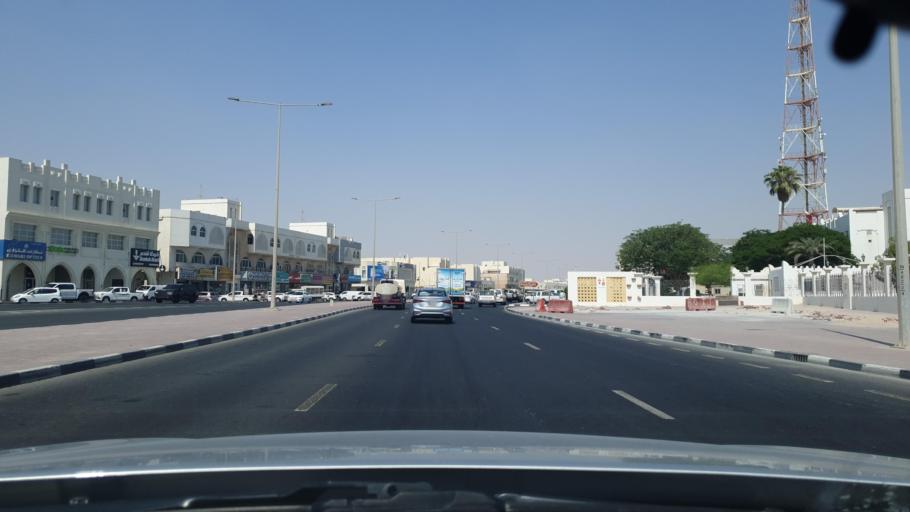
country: QA
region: Al Khawr
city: Al Khawr
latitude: 25.6815
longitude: 51.4966
